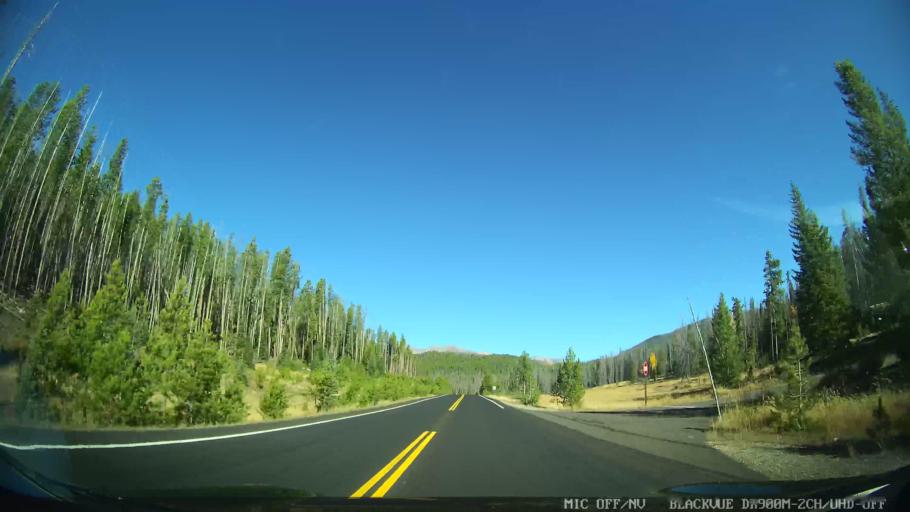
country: US
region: Colorado
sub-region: Grand County
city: Granby
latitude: 40.3153
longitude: -105.8435
